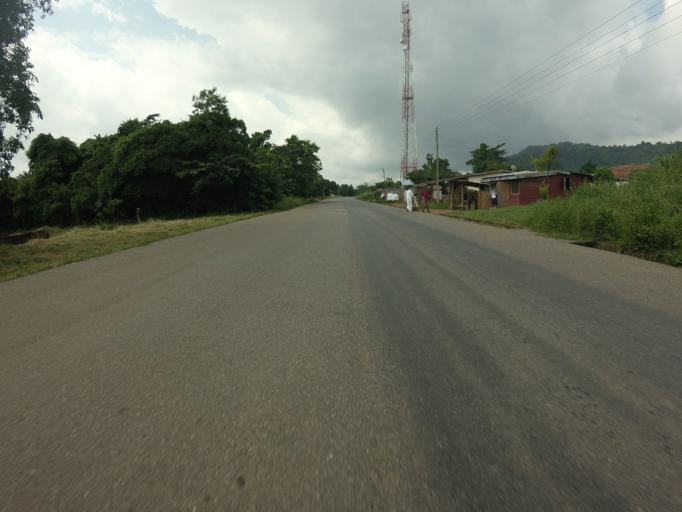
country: GH
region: Volta
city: Kpandu
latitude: 6.9016
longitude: 0.4358
